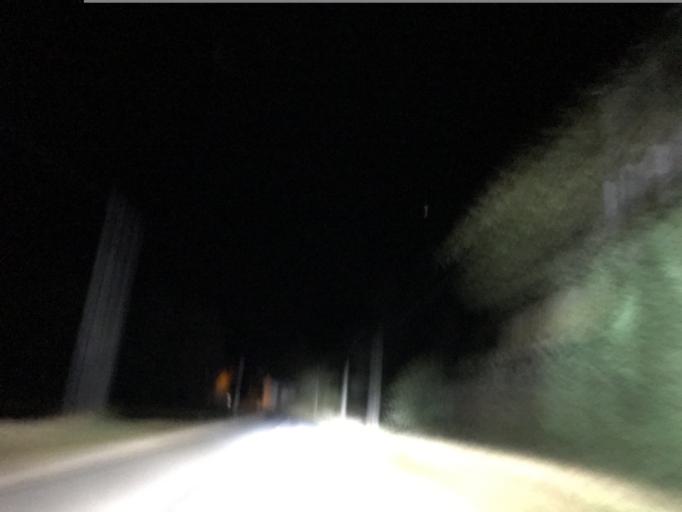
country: FR
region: Auvergne
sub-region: Departement du Puy-de-Dome
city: Celles-sur-Durolle
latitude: 45.8407
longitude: 3.6352
